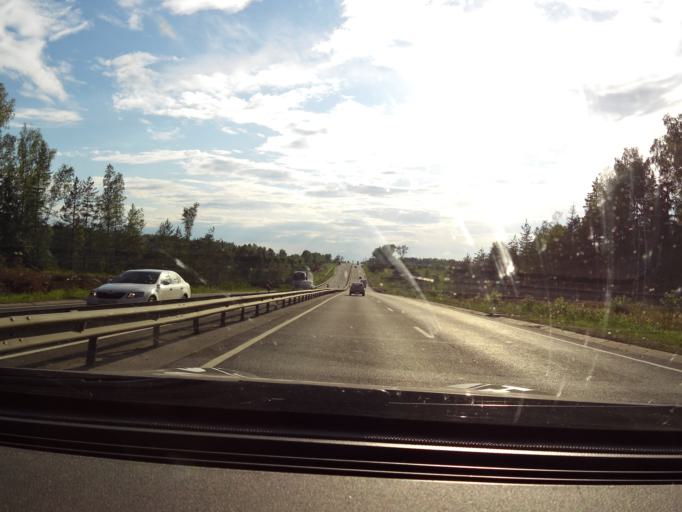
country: RU
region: Vladimir
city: Melekhovo
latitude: 56.2039
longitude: 41.1479
